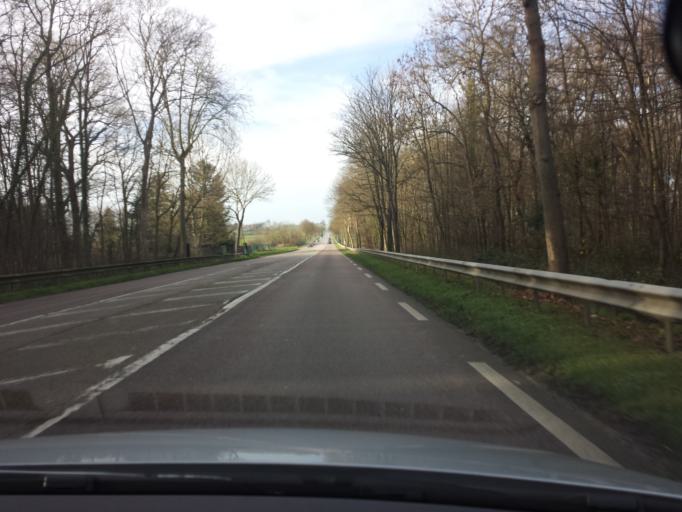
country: FR
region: Haute-Normandie
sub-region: Departement de l'Eure
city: Breuilpont
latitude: 49.0185
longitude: 1.4779
